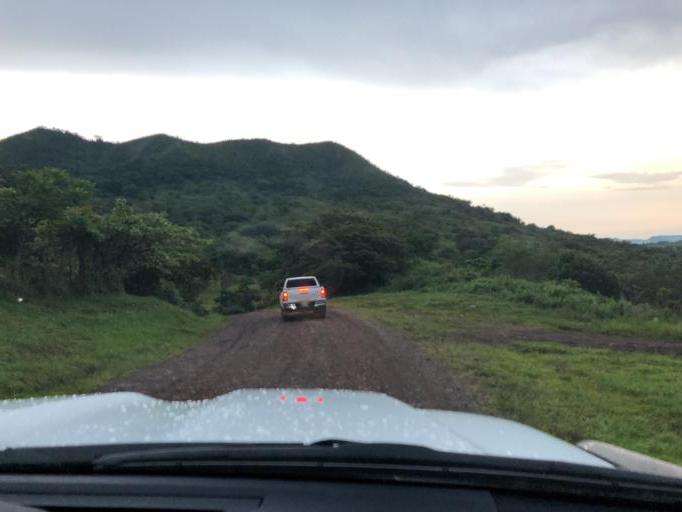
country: NI
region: Chontales
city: La Libertad
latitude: 12.1701
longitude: -85.1772
